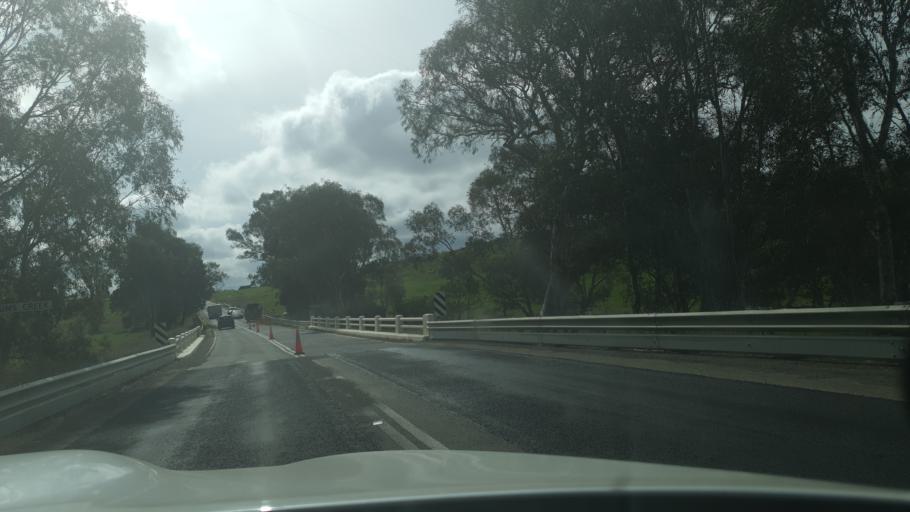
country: AU
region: Victoria
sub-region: Central Goldfields
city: Maryborough
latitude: -37.2140
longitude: 143.7274
